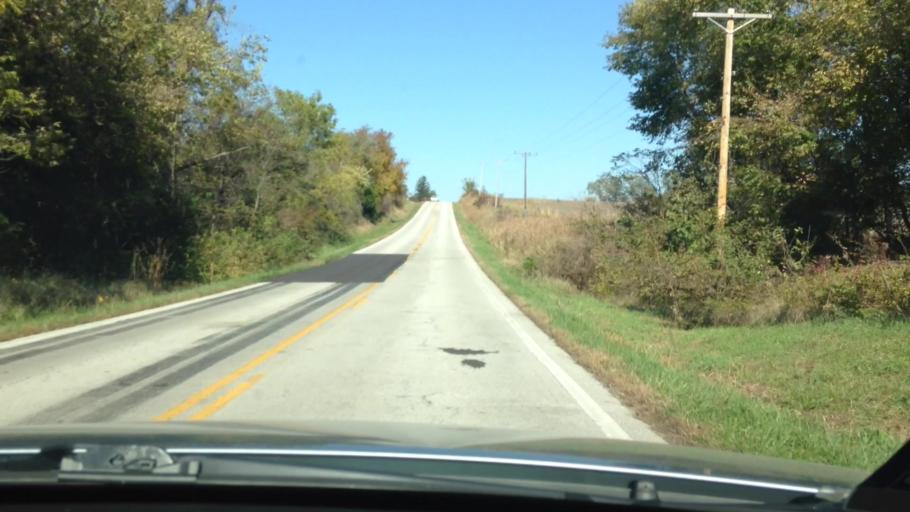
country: US
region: Missouri
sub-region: Platte County
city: Weatherby Lake
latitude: 39.3200
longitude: -94.6488
